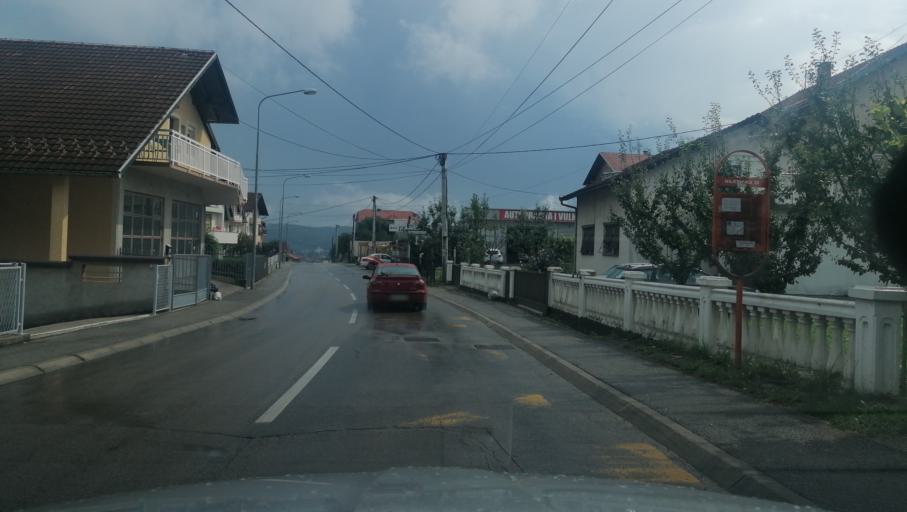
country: BA
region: Republika Srpska
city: Banja Luka
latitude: 44.7909
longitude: 17.1882
